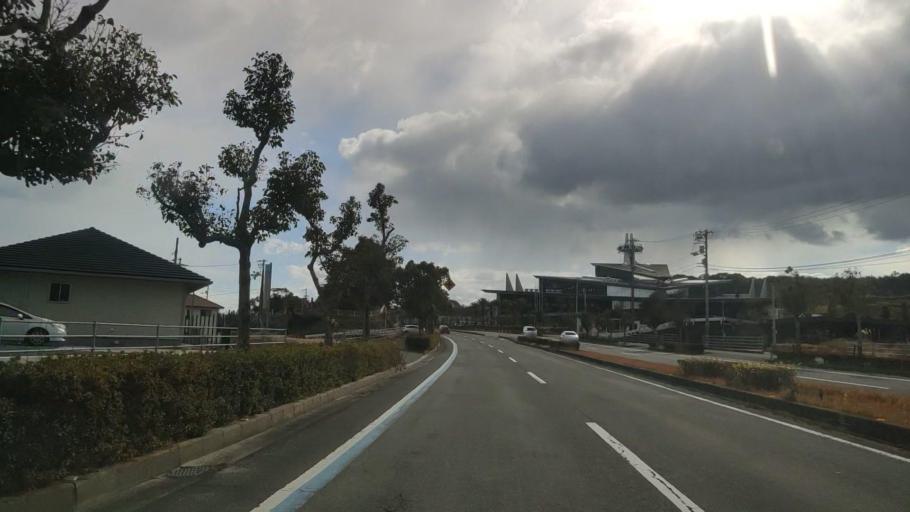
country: JP
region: Ehime
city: Hojo
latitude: 34.0650
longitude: 132.9522
